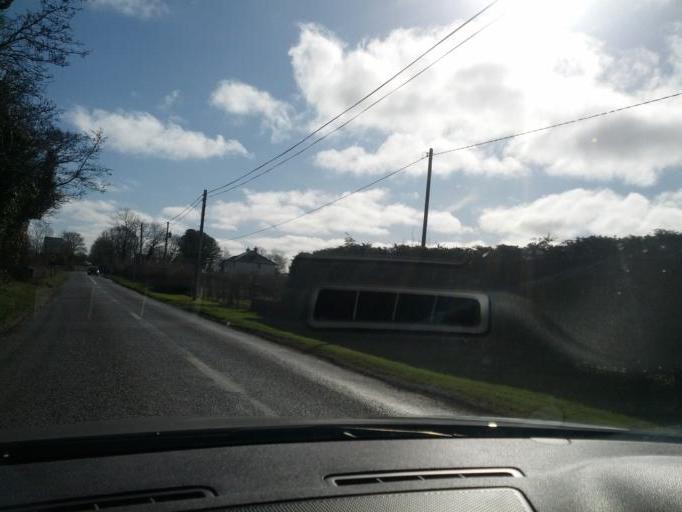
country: IE
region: Connaught
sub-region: County Galway
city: Ballinasloe
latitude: 53.4138
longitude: -8.3511
